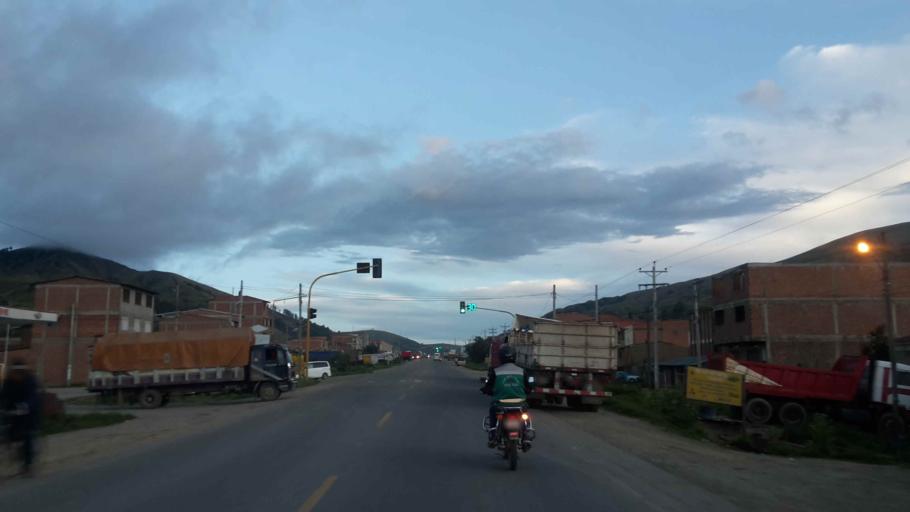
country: BO
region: Cochabamba
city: Colomi
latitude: -17.3353
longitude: -65.8673
